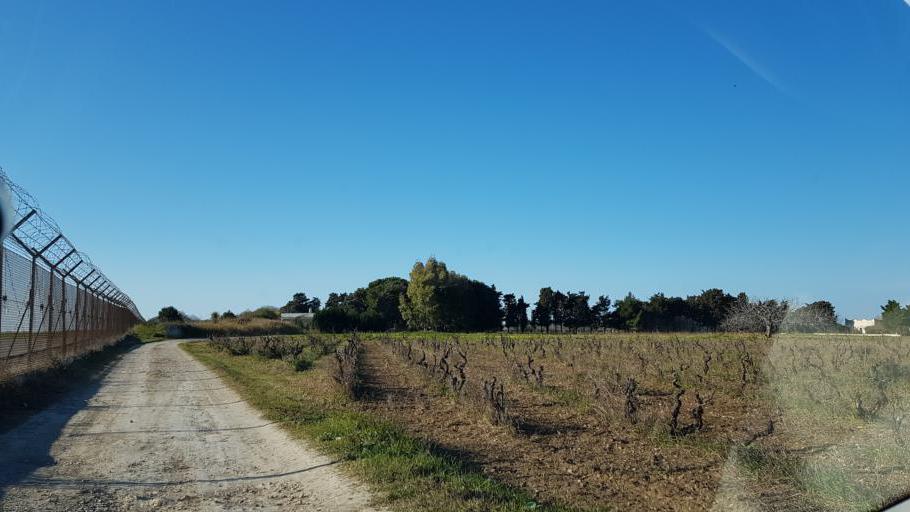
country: IT
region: Apulia
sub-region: Provincia di Brindisi
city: Materdomini
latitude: 40.6690
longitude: 17.9380
